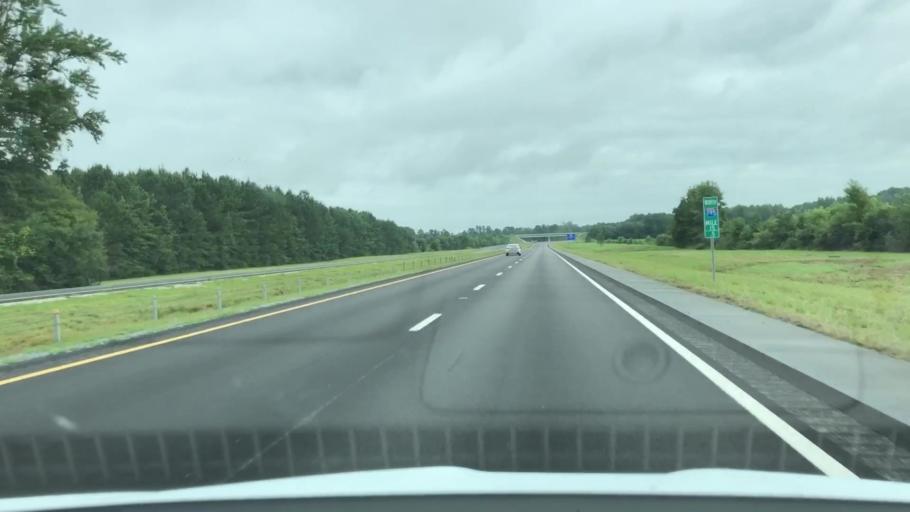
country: US
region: North Carolina
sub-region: Wayne County
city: Fremont
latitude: 35.5323
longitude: -77.9892
